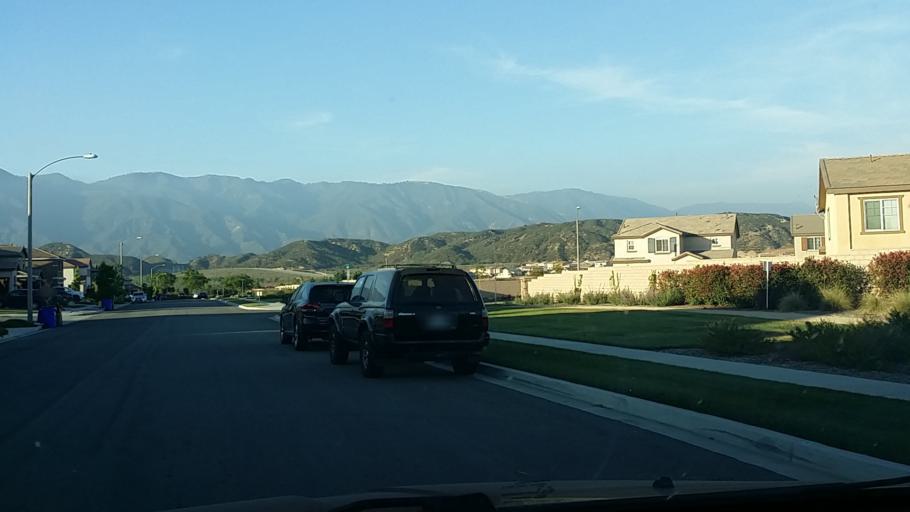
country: US
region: California
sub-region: San Bernardino County
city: Muscoy
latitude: 34.1893
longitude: -117.4222
